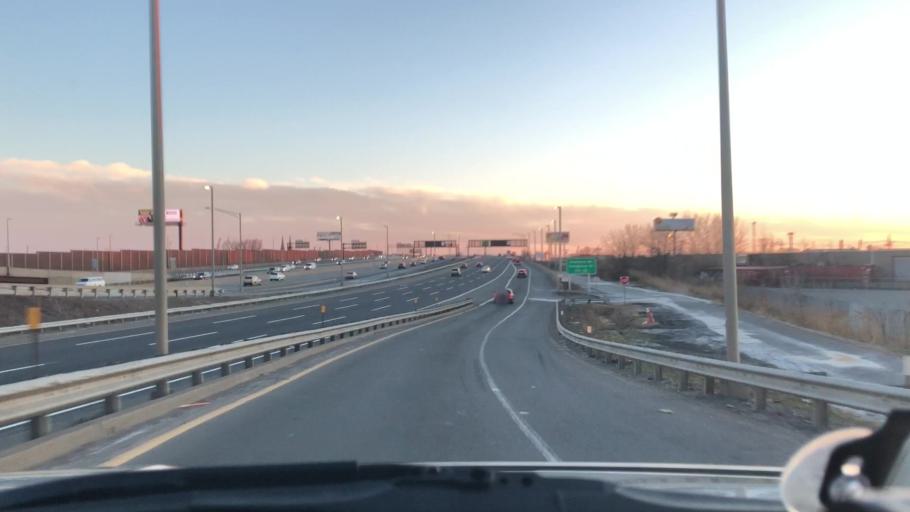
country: US
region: New Jersey
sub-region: Union County
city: Elizabeth
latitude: 40.6647
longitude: -74.1836
